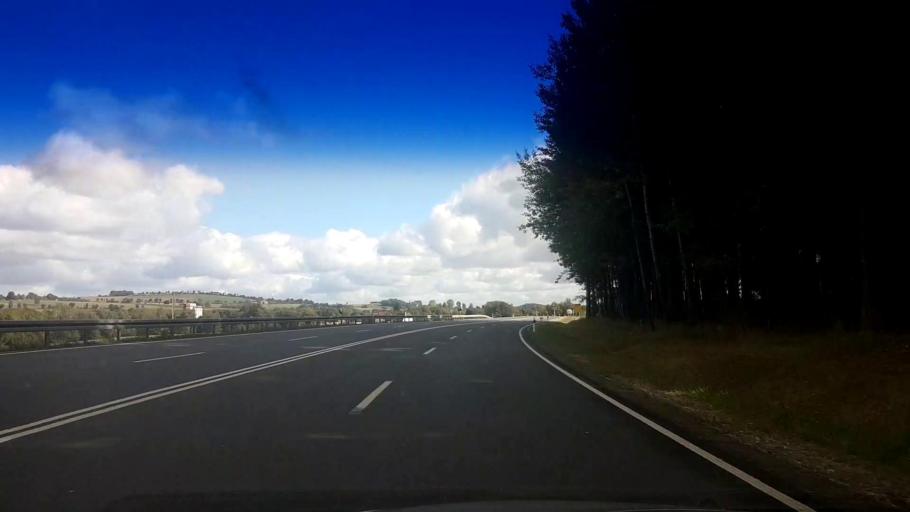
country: DE
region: Bavaria
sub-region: Upper Franconia
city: Trostau
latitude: 50.0164
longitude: 11.9289
